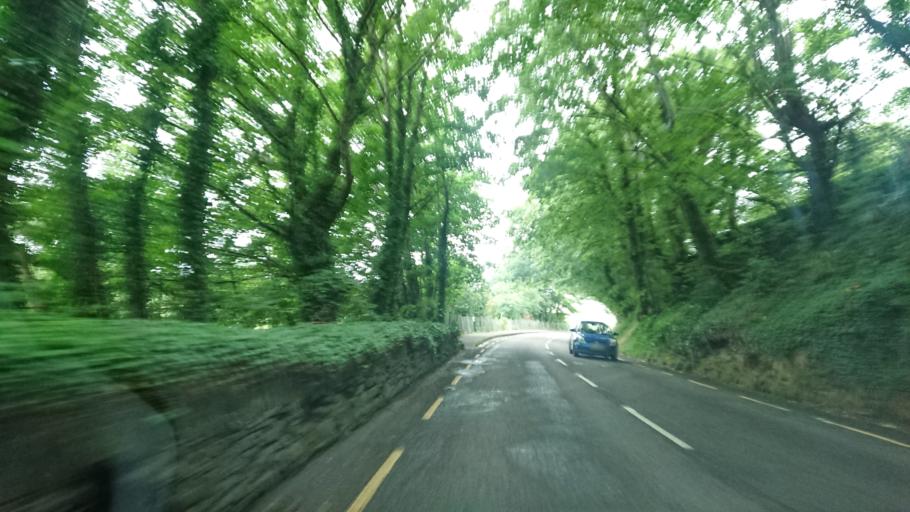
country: IE
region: Munster
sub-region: Ciarrai
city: Killorglin
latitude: 52.1035
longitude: -9.7777
